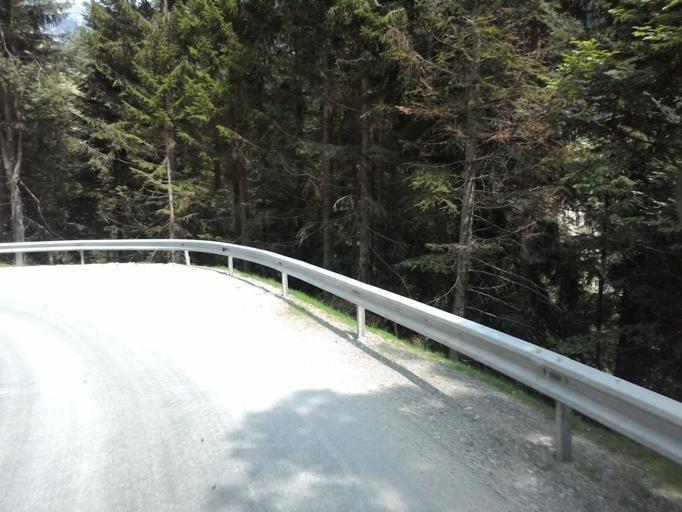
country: AT
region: Tyrol
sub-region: Politischer Bezirk Lienz
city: Untertilliach
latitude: 46.6990
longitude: 12.7734
